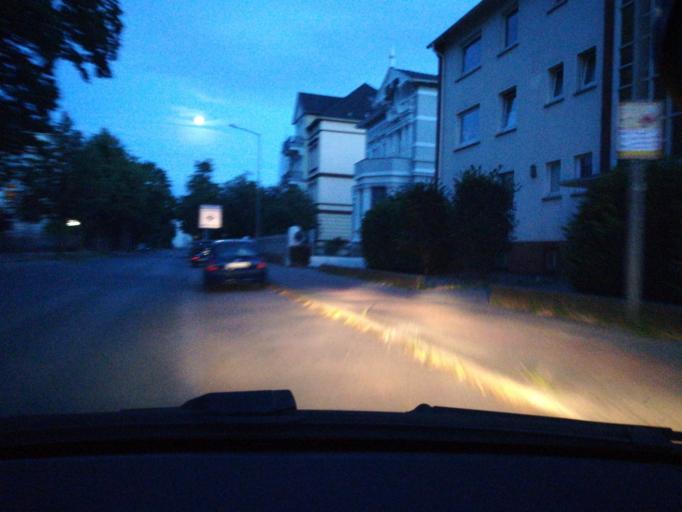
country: DE
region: North Rhine-Westphalia
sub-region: Regierungsbezirk Detmold
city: Minden
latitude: 52.2968
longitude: 8.9120
